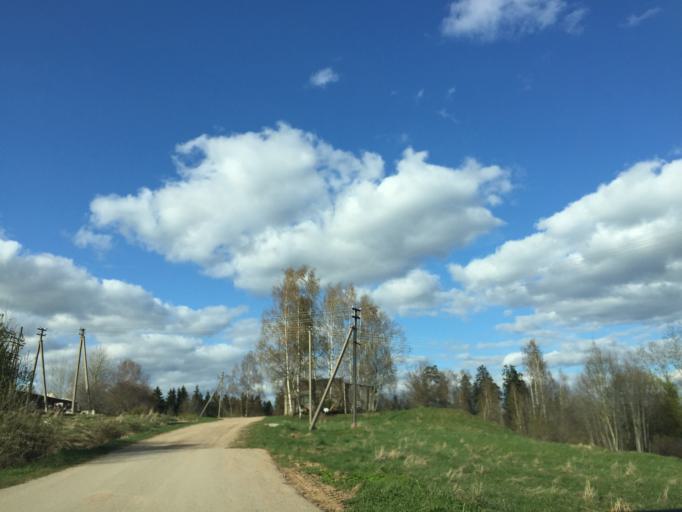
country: LV
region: Rezekne
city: Rezekne
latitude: 56.6433
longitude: 27.3898
